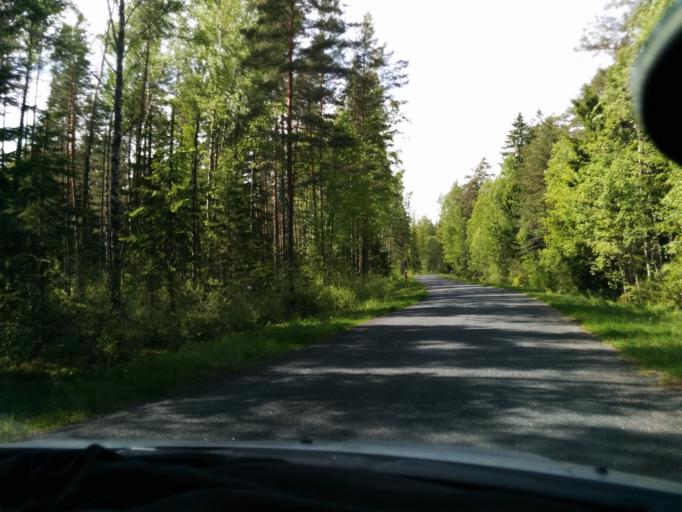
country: EE
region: Harju
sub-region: Loksa linn
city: Loksa
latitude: 59.5661
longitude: 25.6297
